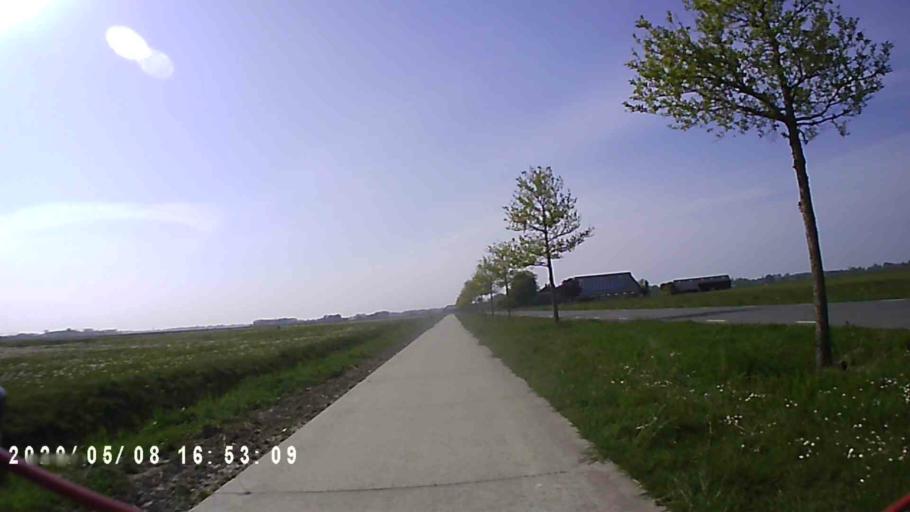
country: NL
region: Groningen
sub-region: Gemeente Bedum
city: Bedum
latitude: 53.3864
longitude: 6.6265
